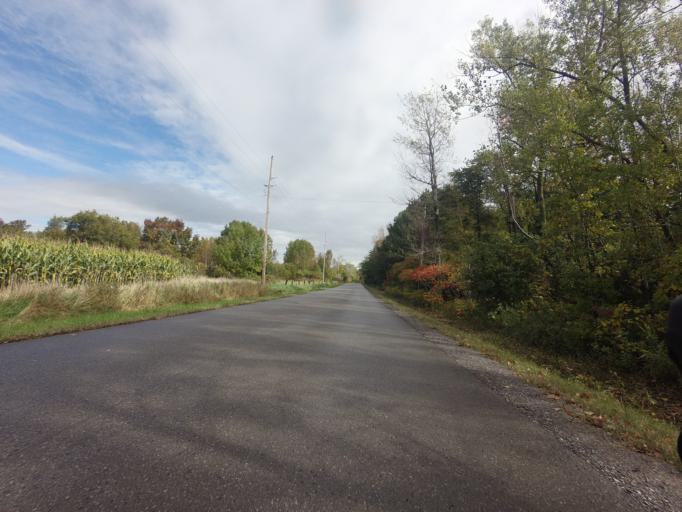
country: CA
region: Ontario
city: Cobourg
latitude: 43.9223
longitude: -78.4228
